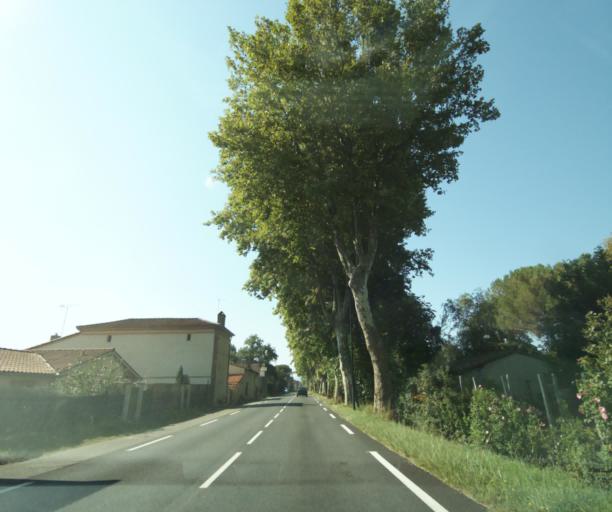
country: FR
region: Midi-Pyrenees
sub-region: Departement de la Haute-Garonne
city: Saint-Sulpice-sur-Leze
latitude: 43.3329
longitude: 1.3220
